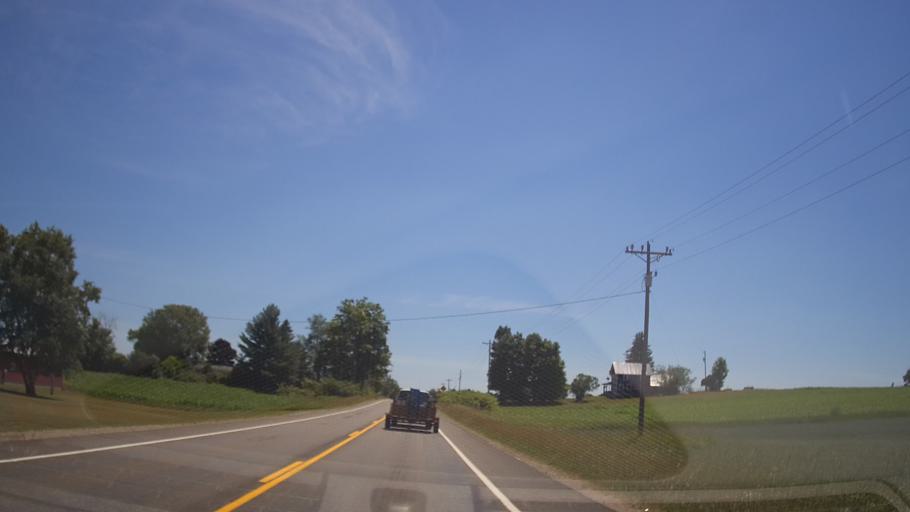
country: US
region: Michigan
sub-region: Grand Traverse County
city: Kingsley
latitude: 44.6038
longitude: -85.6965
